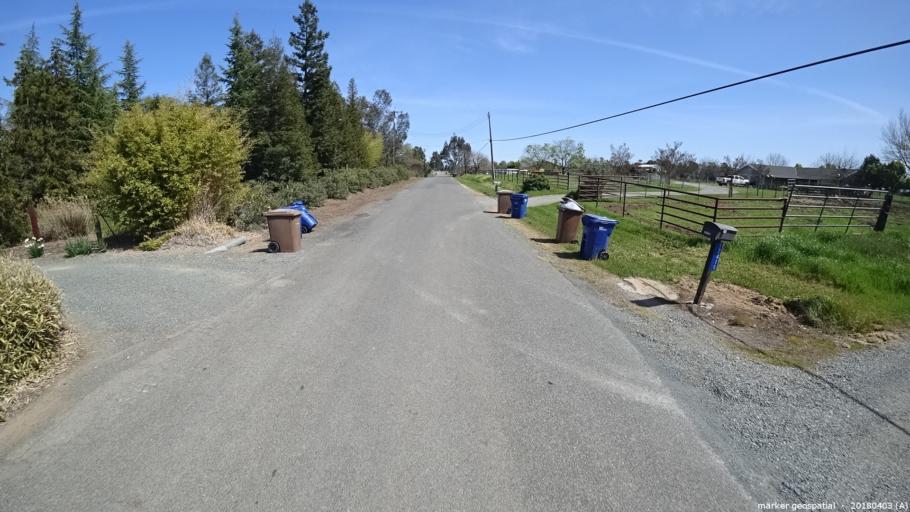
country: US
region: California
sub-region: Sacramento County
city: Clay
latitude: 38.3578
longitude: -121.2089
